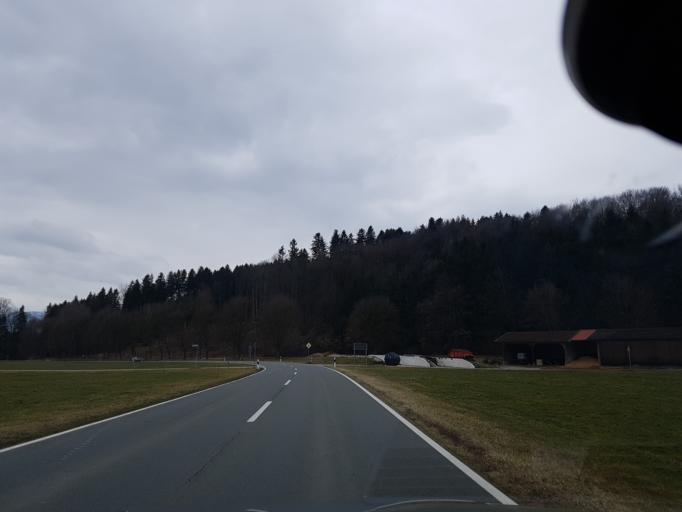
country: DE
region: Bavaria
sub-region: Upper Bavaria
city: Bad Aibling
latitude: 47.8428
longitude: 11.9782
